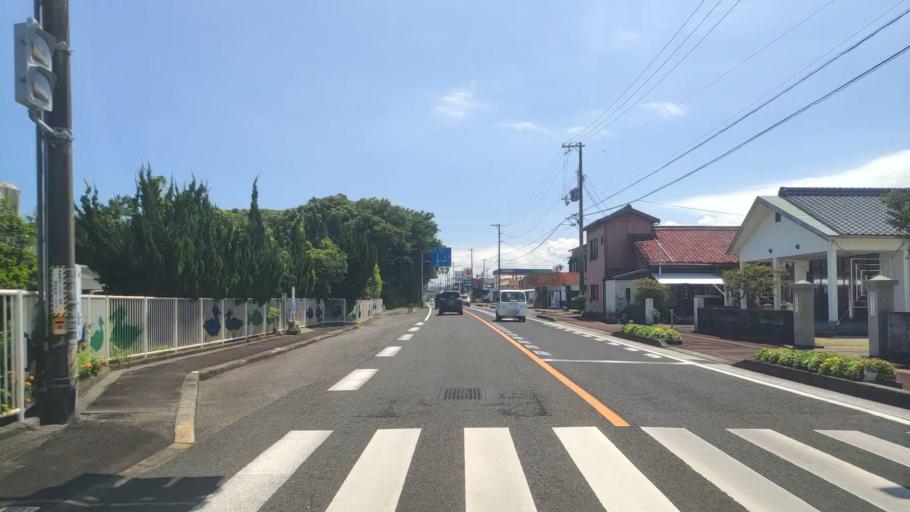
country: JP
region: Wakayama
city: Shingu
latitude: 33.8722
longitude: 136.0857
